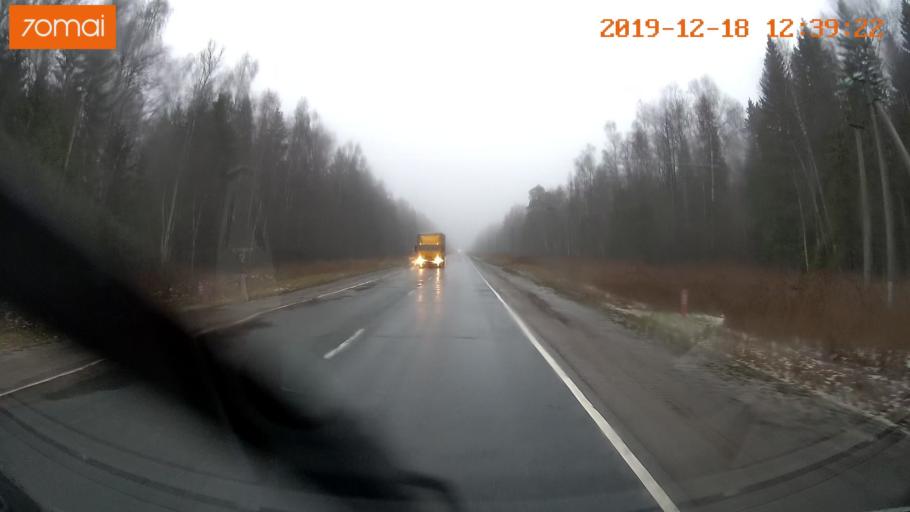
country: RU
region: Moskovskaya
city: Vysokovsk
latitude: 56.1640
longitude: 36.6110
